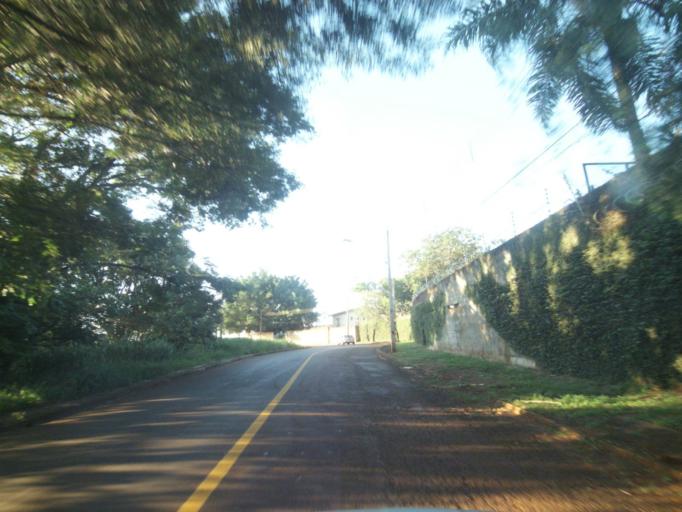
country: BR
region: Parana
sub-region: Londrina
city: Londrina
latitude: -23.3477
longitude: -51.1948
